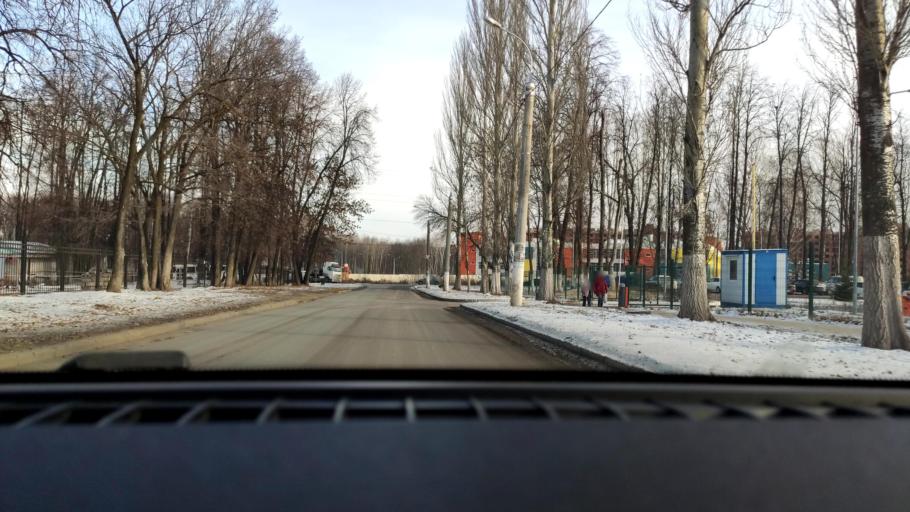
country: RU
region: Samara
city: Petra-Dubrava
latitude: 53.3067
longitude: 50.2771
